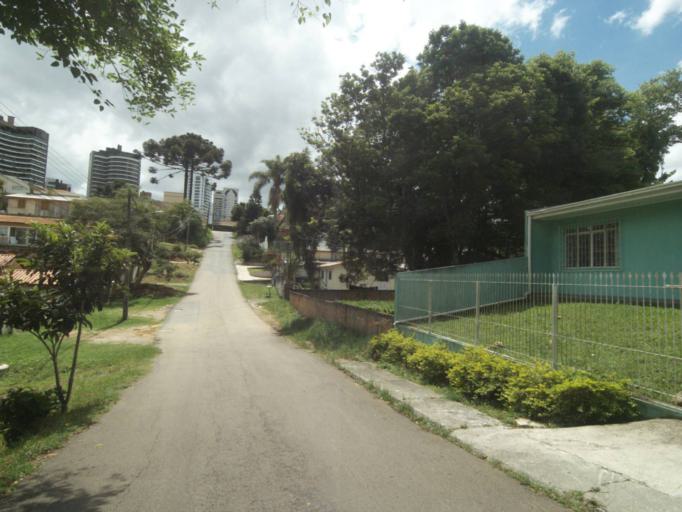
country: BR
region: Parana
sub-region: Curitiba
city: Curitiba
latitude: -25.4360
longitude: -49.3221
